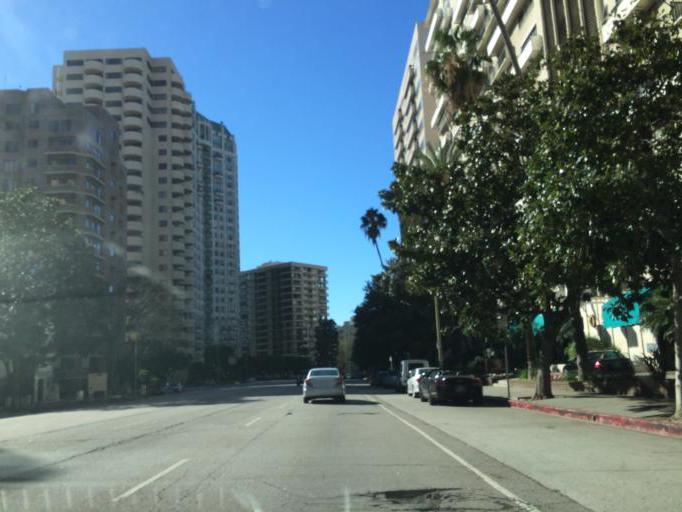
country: US
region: California
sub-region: Los Angeles County
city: Westwood, Los Angeles
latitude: 34.0637
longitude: -118.4324
